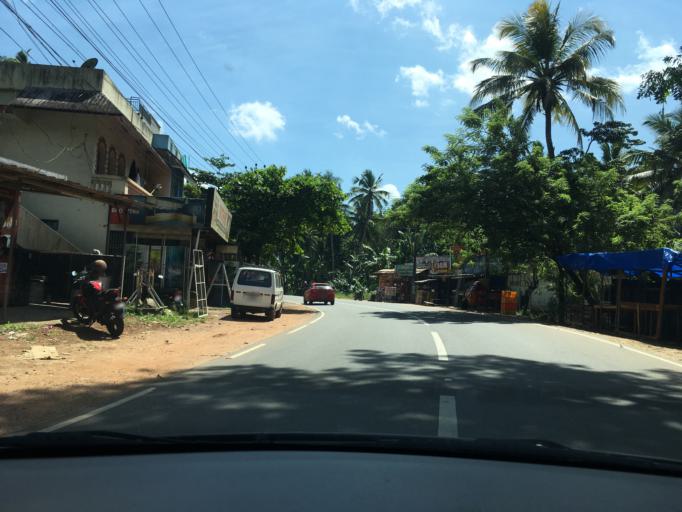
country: IN
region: Kerala
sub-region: Thiruvananthapuram
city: Nedumangad
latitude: 8.5772
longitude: 76.9960
